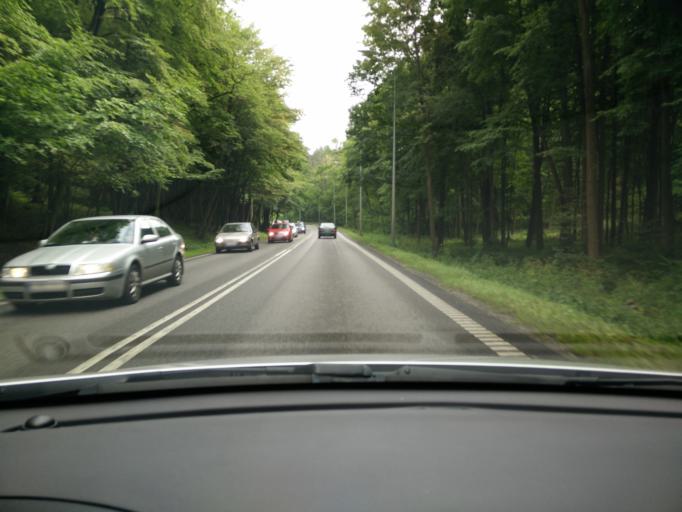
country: PL
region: Pomeranian Voivodeship
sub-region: Gdynia
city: Wielki Kack
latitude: 54.4261
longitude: 18.5026
